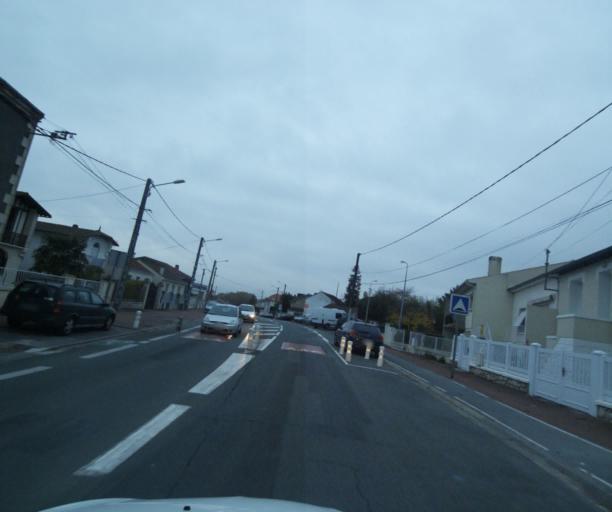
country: FR
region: Poitou-Charentes
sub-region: Departement de la Charente-Maritime
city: Saintes
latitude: 45.7460
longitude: -0.6068
